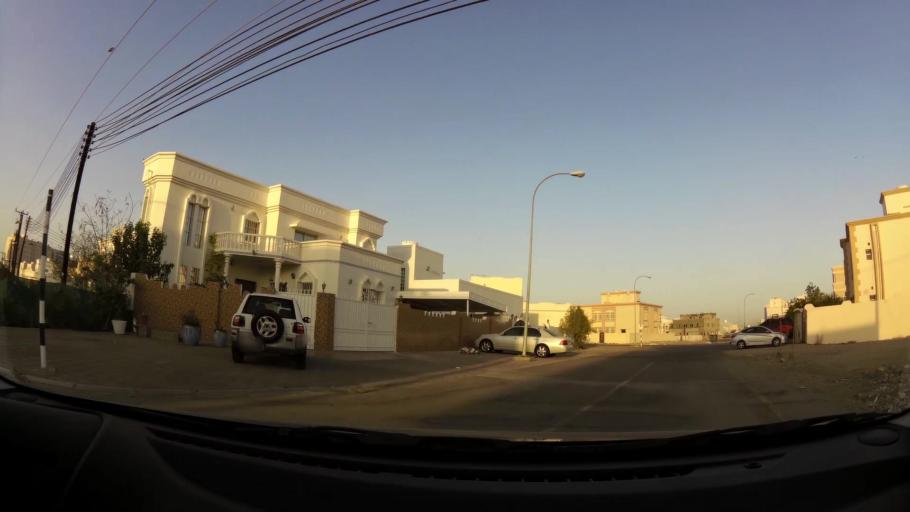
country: OM
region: Muhafazat Masqat
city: As Sib al Jadidah
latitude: 23.6121
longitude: 58.1983
